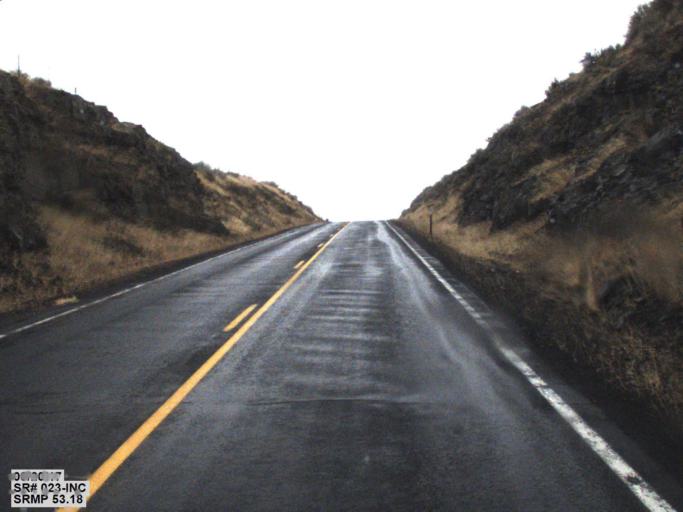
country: US
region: Washington
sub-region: Lincoln County
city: Davenport
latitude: 47.3649
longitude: -118.1113
